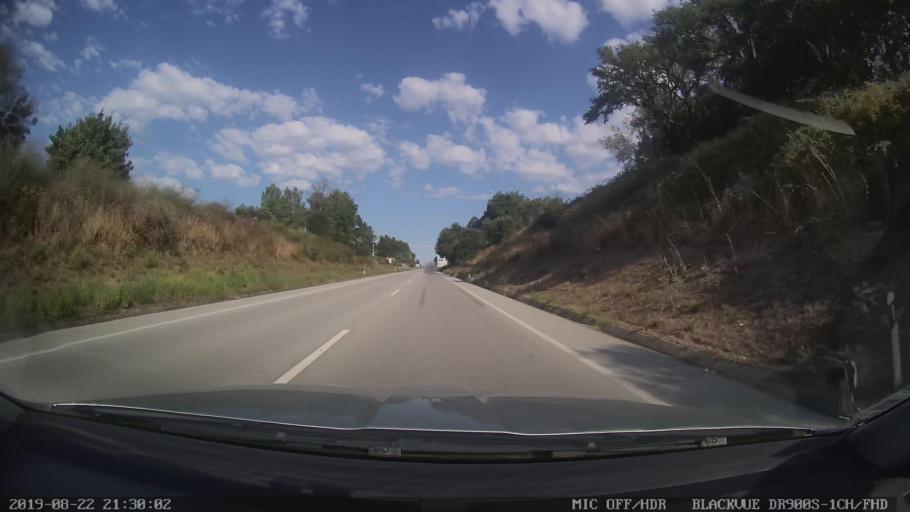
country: PT
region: Leiria
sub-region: Pedrogao Grande
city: Pedrogao Grande
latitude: 39.9068
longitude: -8.1448
